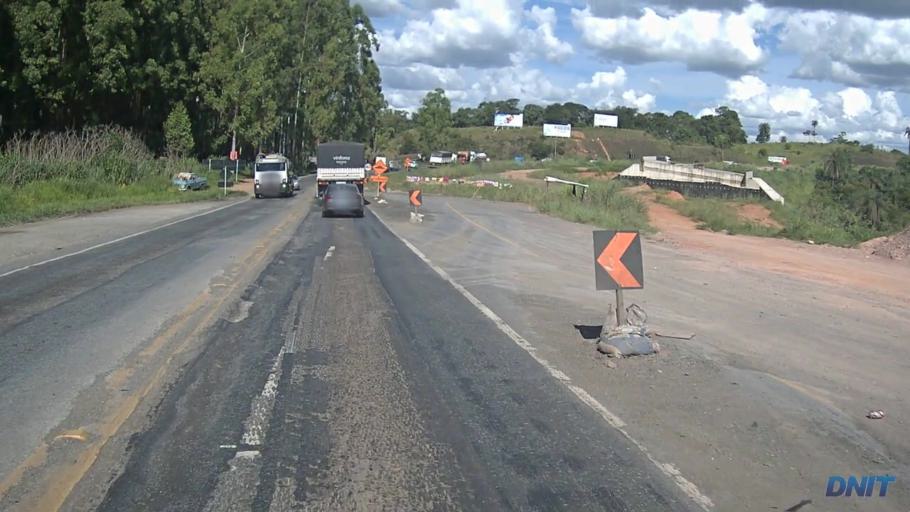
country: BR
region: Minas Gerais
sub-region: Caete
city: Caete
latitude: -19.7478
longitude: -43.6242
